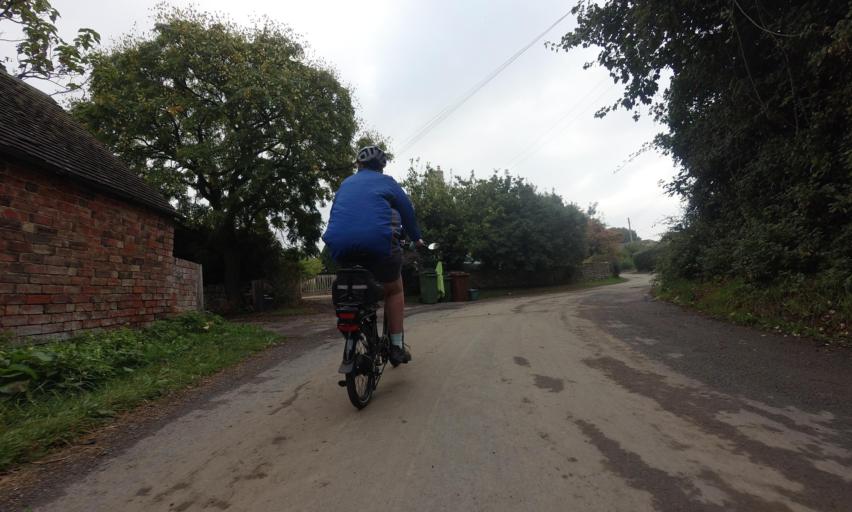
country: GB
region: England
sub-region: Gloucestershire
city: Gotherington
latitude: 51.9896
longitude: -2.0258
